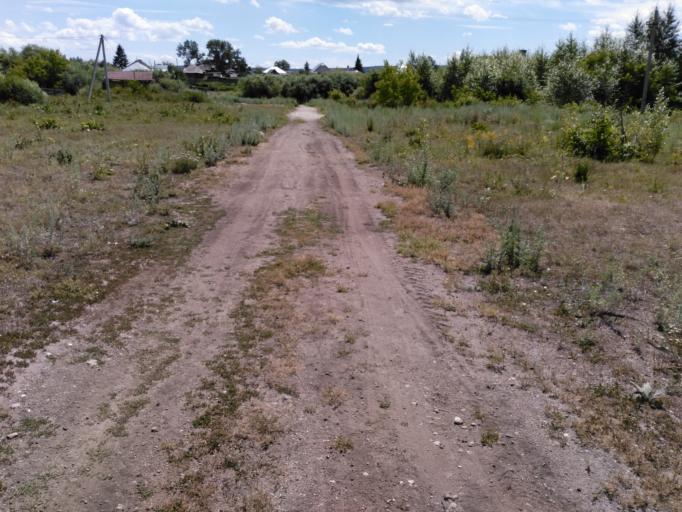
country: RU
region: Bashkortostan
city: Akhunovo
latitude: 54.2105
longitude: 59.5992
